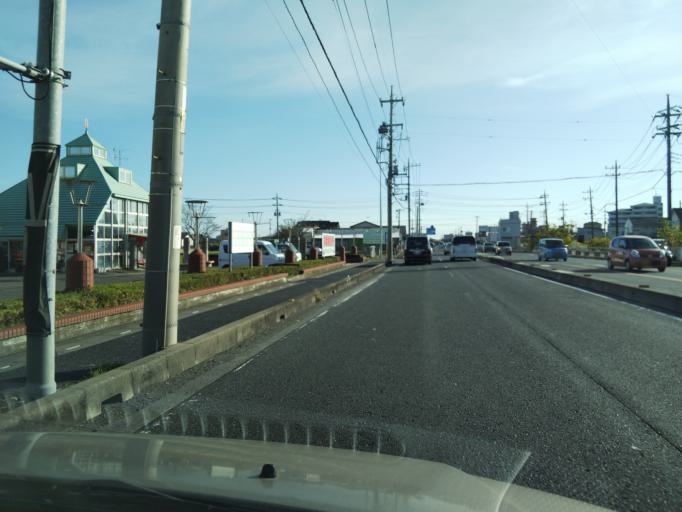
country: JP
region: Saitama
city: Yoshikawa
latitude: 35.8793
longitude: 139.8471
